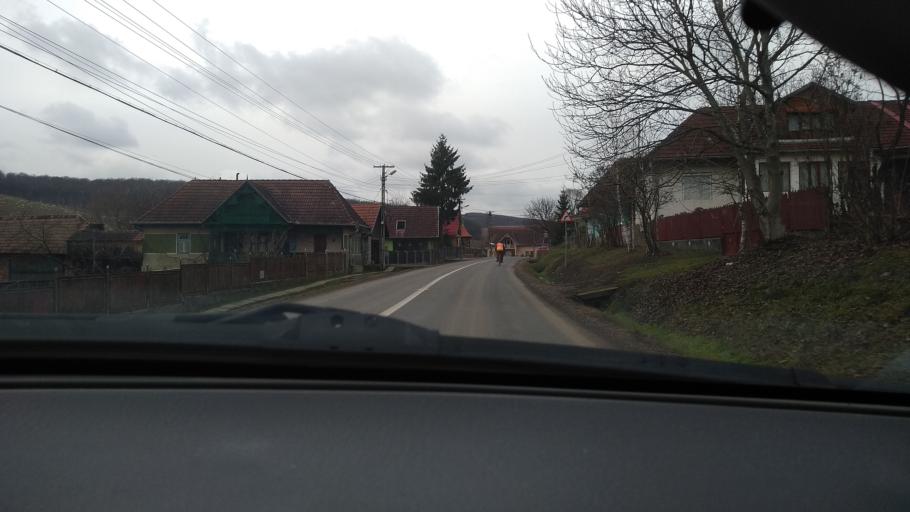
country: RO
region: Mures
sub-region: Comuna Galesti
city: Galesti
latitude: 46.5349
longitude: 24.7613
